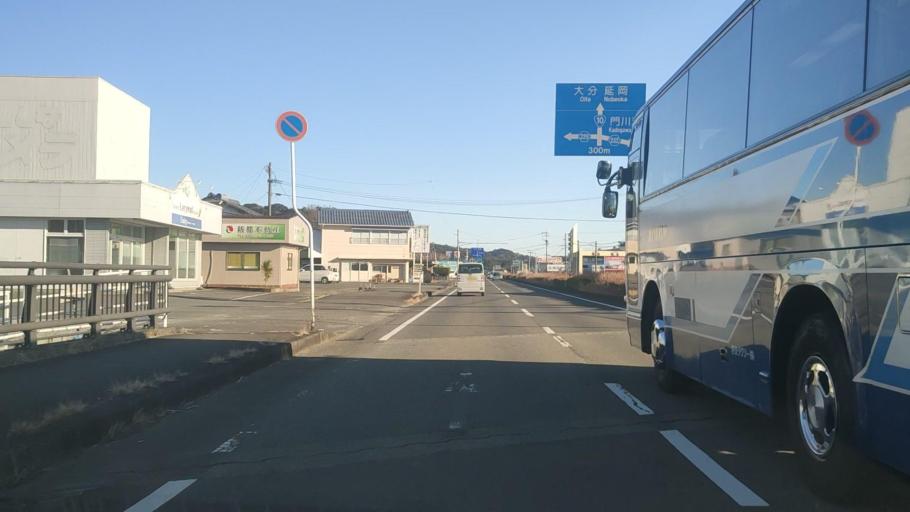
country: JP
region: Miyazaki
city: Nobeoka
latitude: 32.4771
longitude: 131.6545
